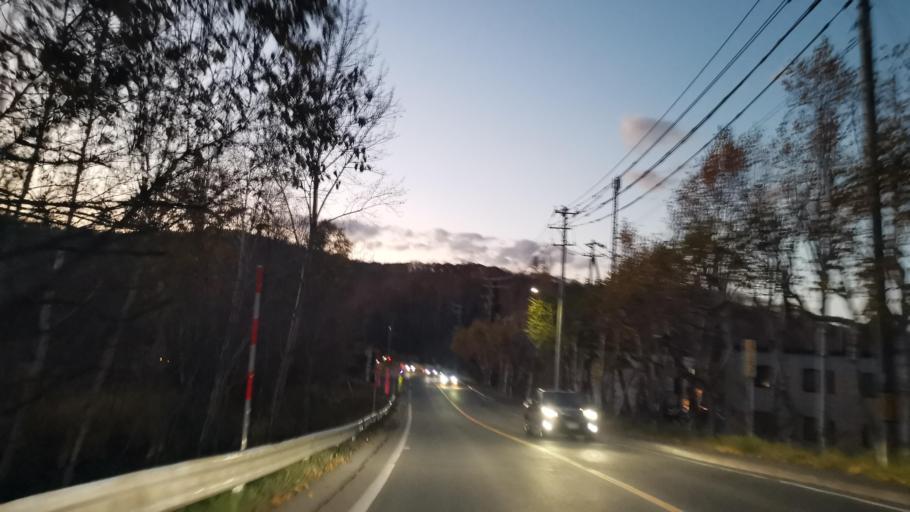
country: JP
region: Hokkaido
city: Sapporo
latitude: 42.9946
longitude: 141.3656
